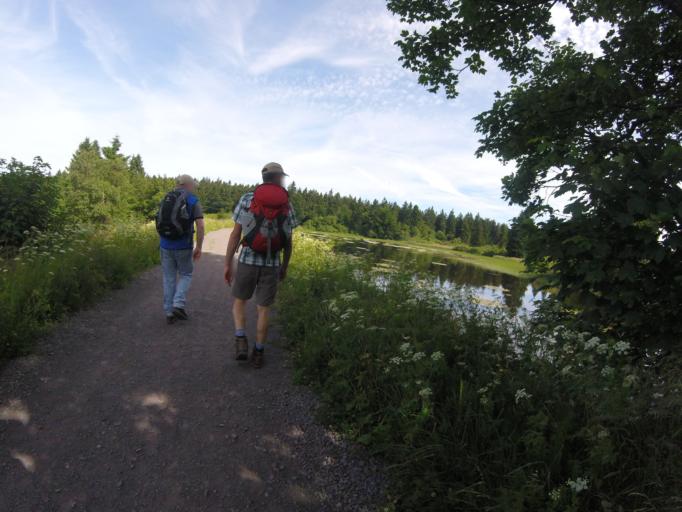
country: DE
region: Hesse
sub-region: Regierungsbezirk Giessen
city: Ulrichstein
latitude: 50.5223
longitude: 9.2293
